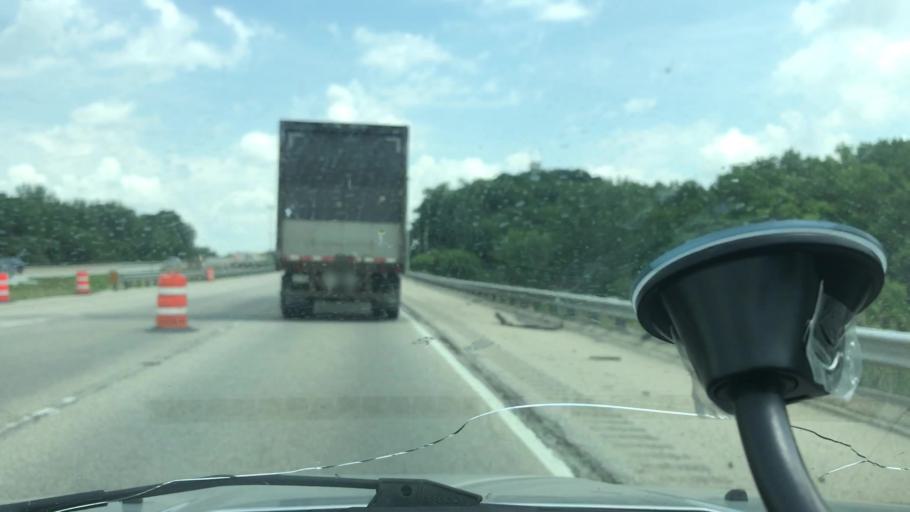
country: US
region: Illinois
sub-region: Peoria County
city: Bellevue
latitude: 40.7319
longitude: -89.6724
